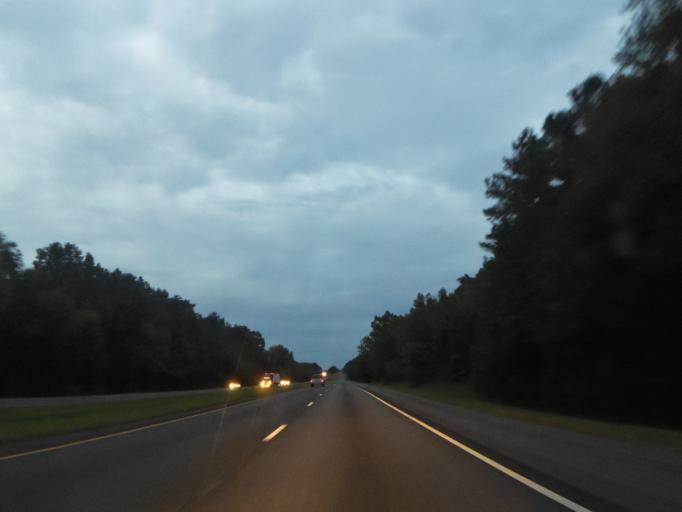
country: US
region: Alabama
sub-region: Etowah County
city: Whitesboro
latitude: 34.1806
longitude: -85.9603
